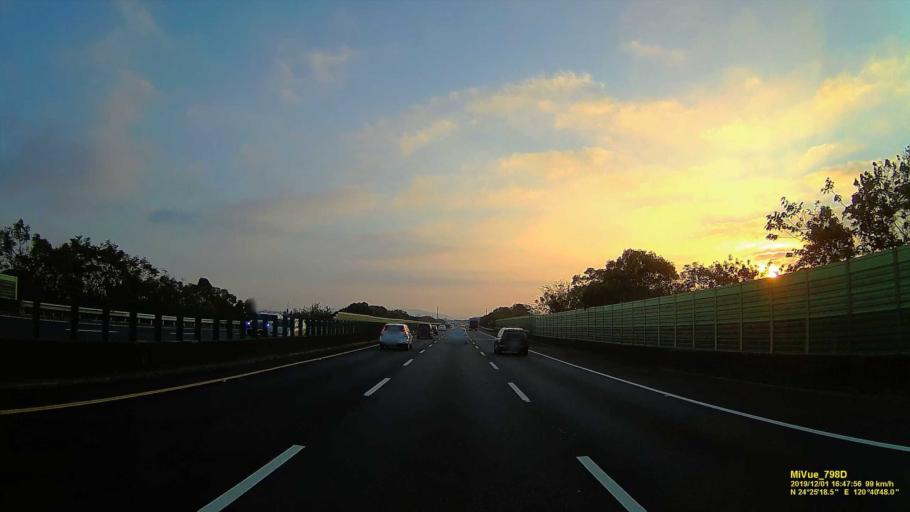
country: TW
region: Taiwan
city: Fengyuan
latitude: 24.4207
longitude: 120.6796
